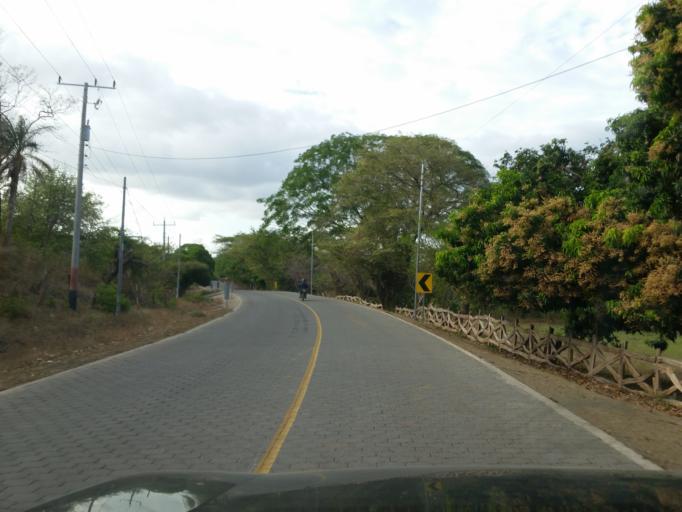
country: NI
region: Rivas
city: Tola
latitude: 11.4311
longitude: -85.9430
